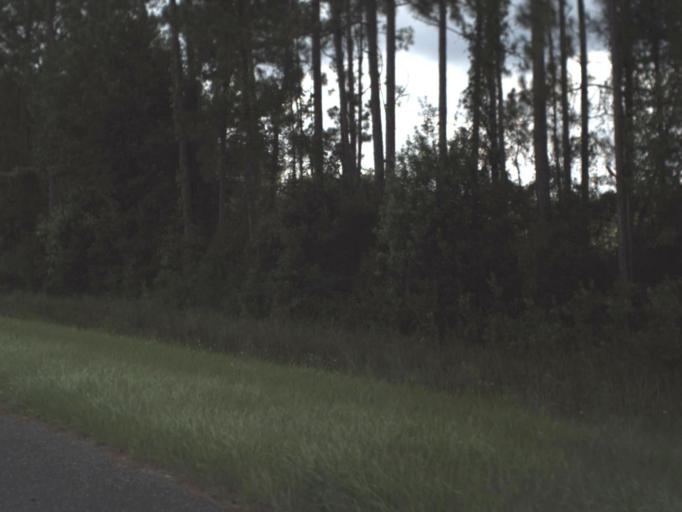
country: US
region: Florida
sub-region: Levy County
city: Bronson
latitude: 29.4590
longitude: -82.6586
